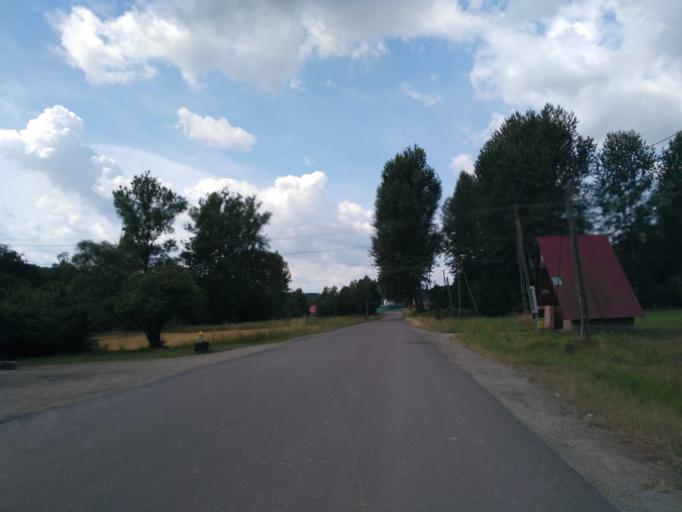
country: PL
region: Subcarpathian Voivodeship
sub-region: Powiat debicki
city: Brzostek
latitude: 49.9219
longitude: 21.3837
